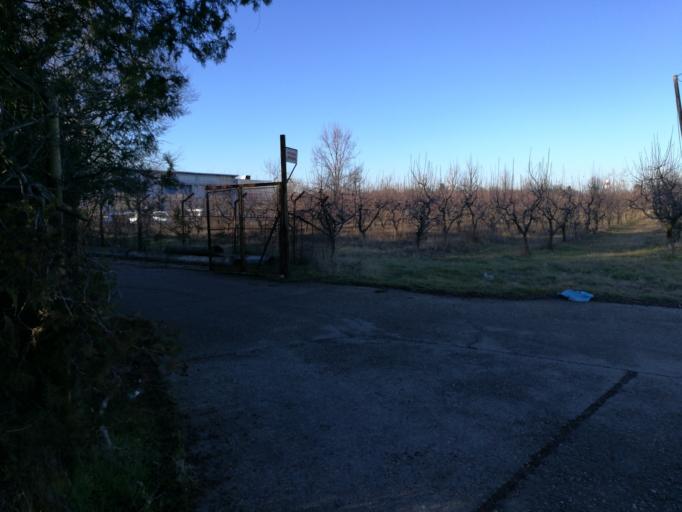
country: RO
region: Ilfov
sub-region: Comuna Otopeni
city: Otopeni
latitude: 44.5020
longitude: 26.0768
